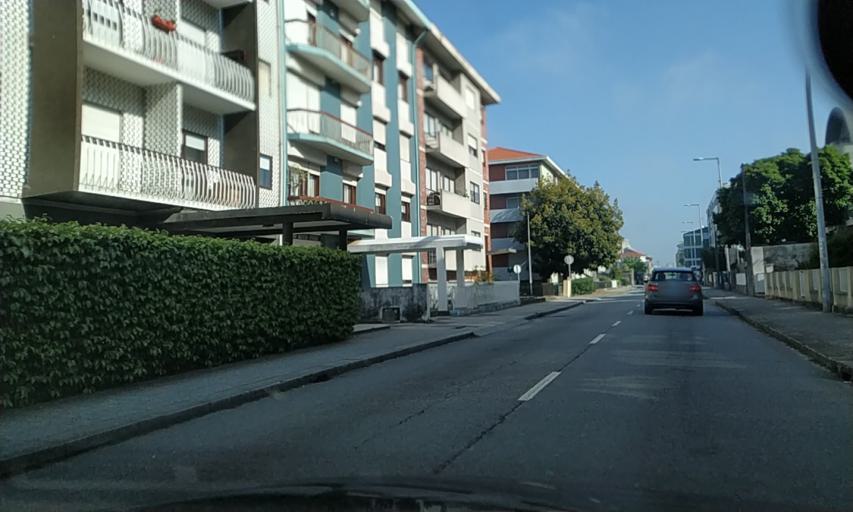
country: PT
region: Porto
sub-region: Porto
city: Porto
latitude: 41.1614
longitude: -8.6247
